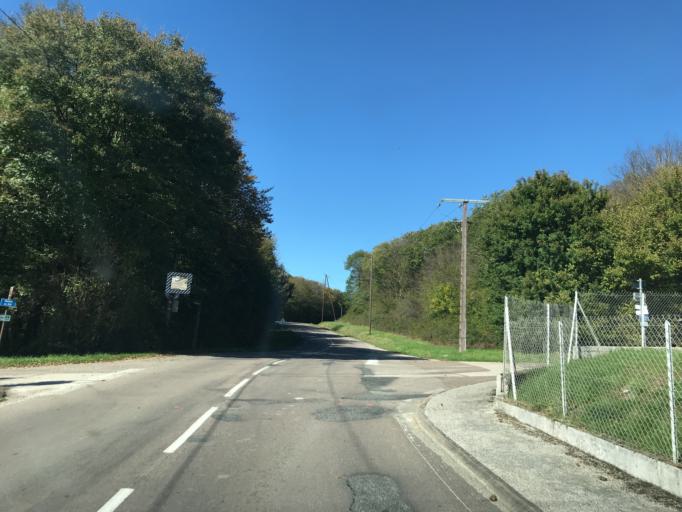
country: FR
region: Franche-Comte
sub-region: Departement du Doubs
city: Thise
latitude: 47.2859
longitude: 6.0675
